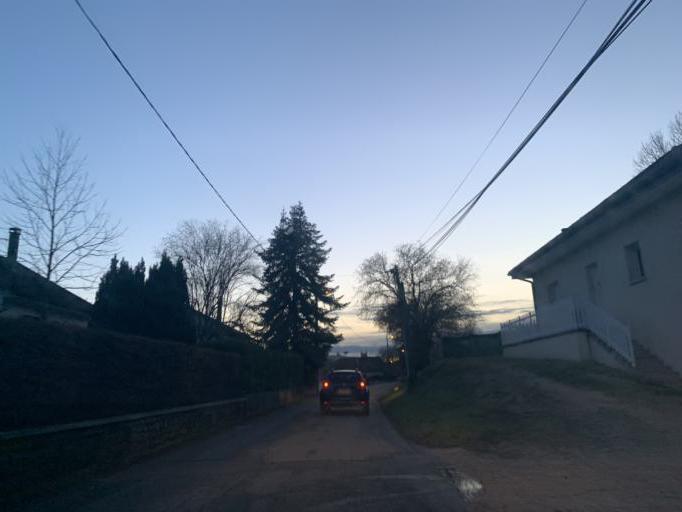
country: FR
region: Rhone-Alpes
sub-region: Departement de l'Ain
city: Belley
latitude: 45.7637
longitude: 5.6972
